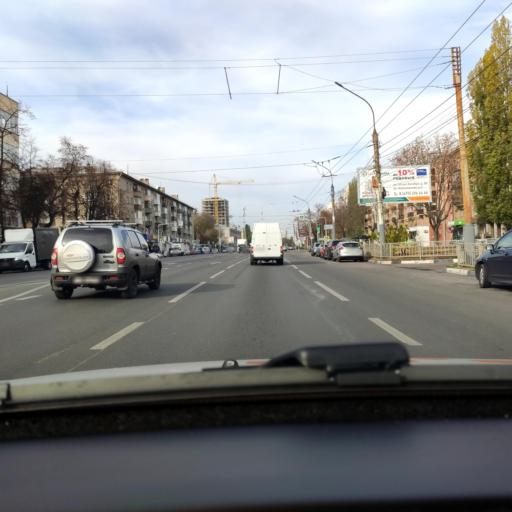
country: RU
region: Voronezj
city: Voronezh
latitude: 51.6452
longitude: 39.1993
